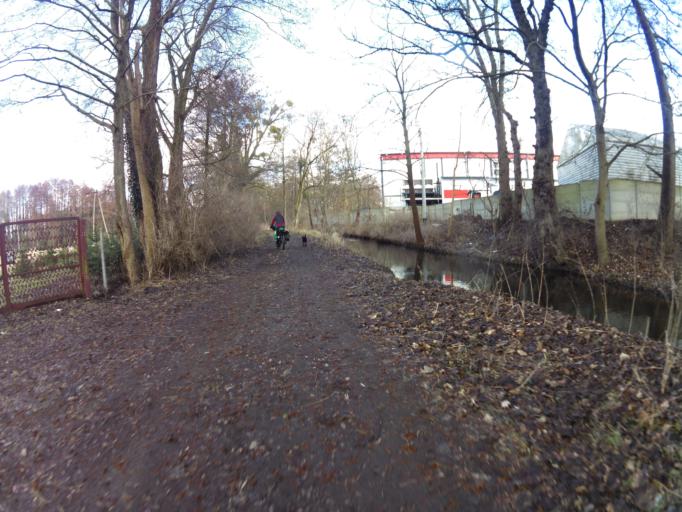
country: PL
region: West Pomeranian Voivodeship
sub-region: Powiat mysliborski
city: Debno
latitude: 52.7462
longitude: 14.7111
